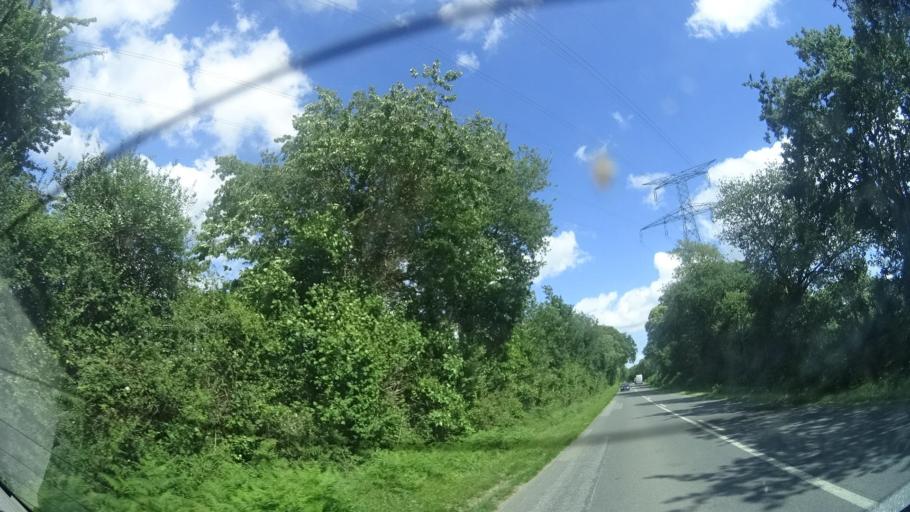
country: FR
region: Brittany
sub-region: Departement du Morbihan
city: Pluherlin
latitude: 47.6777
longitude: -2.3838
